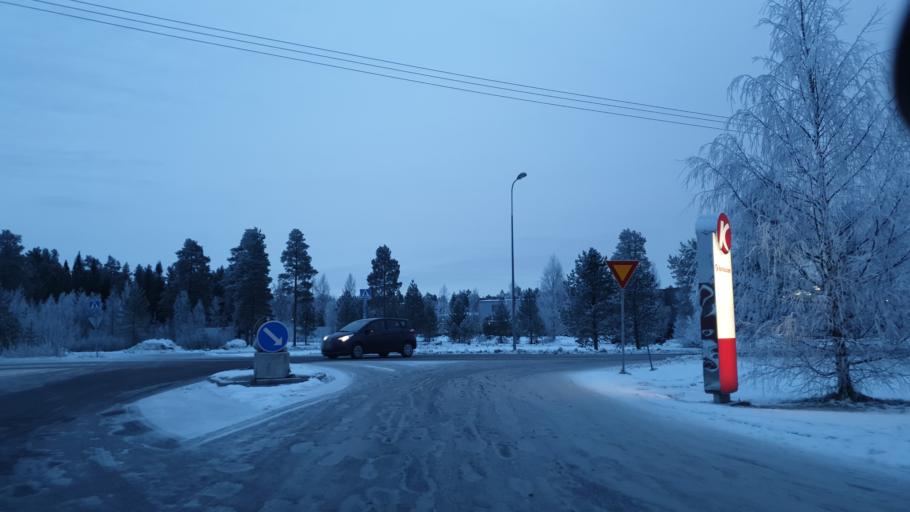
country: FI
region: Northern Ostrobothnia
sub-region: Oulunkaari
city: Ii
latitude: 65.2898
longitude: 25.3764
